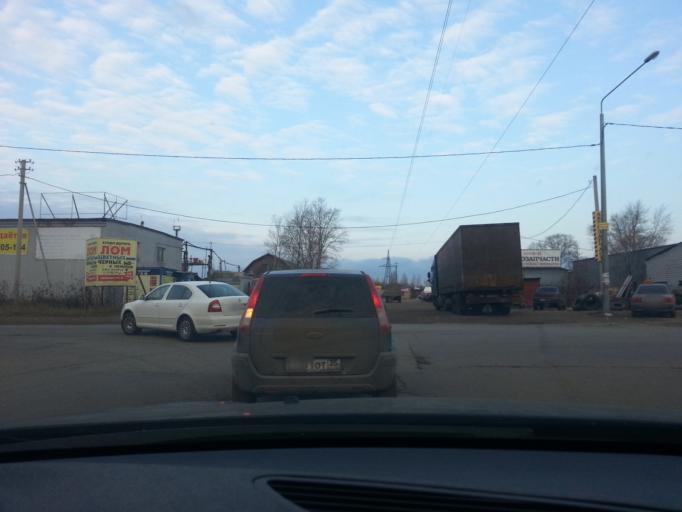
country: RU
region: Vologda
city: Vologda
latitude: 59.2314
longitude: 39.9308
